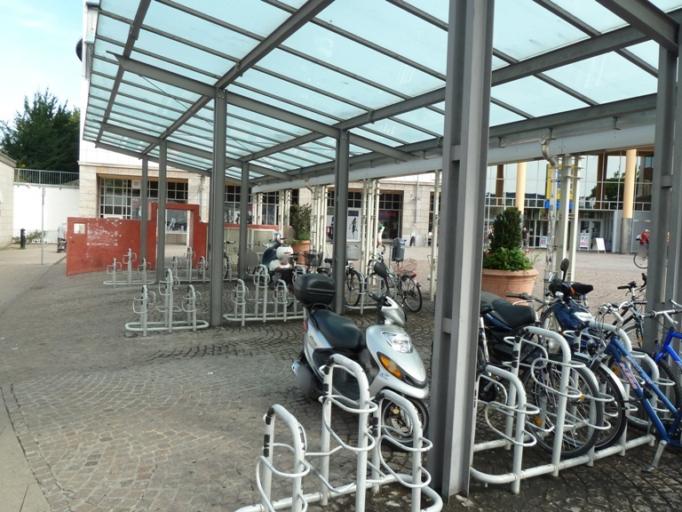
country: DE
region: Baden-Wuerttemberg
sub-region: Tuebingen Region
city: Friedrichshafen
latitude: 47.6518
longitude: 9.4824
